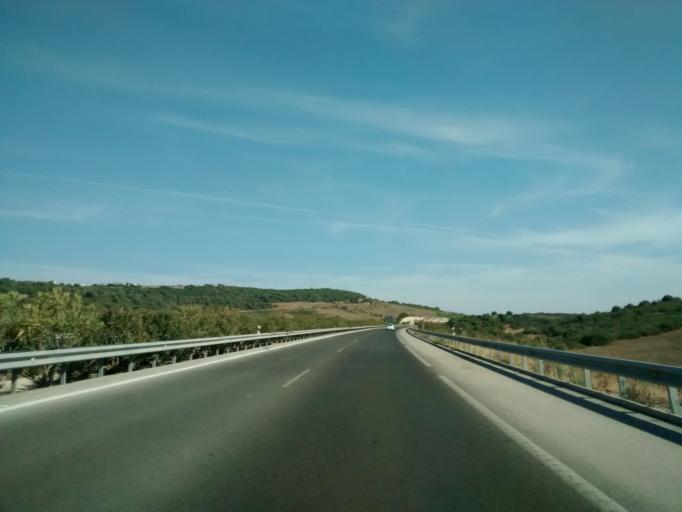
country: ES
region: Andalusia
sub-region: Provincia de Cadiz
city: Conil de la Frontera
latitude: 36.3143
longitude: -6.0570
